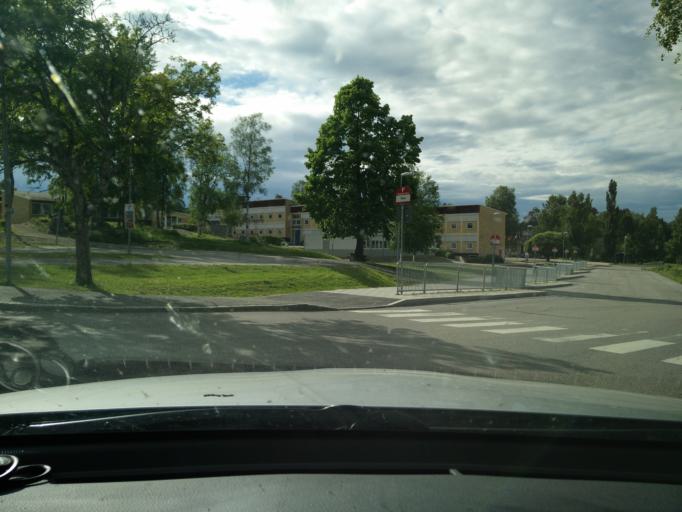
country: SE
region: Gaevleborg
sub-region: Nordanstigs Kommun
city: Bergsjoe
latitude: 61.9825
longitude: 17.0582
